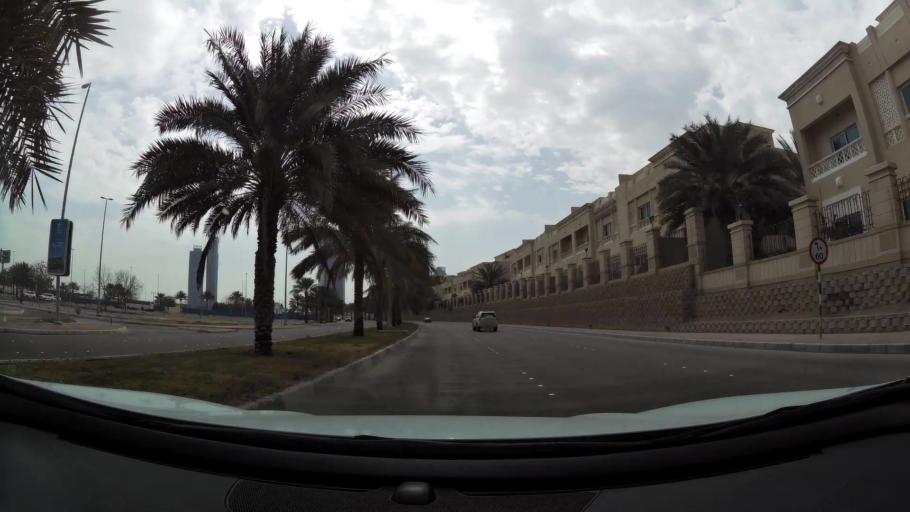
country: AE
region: Abu Dhabi
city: Abu Dhabi
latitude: 24.4747
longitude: 54.3188
